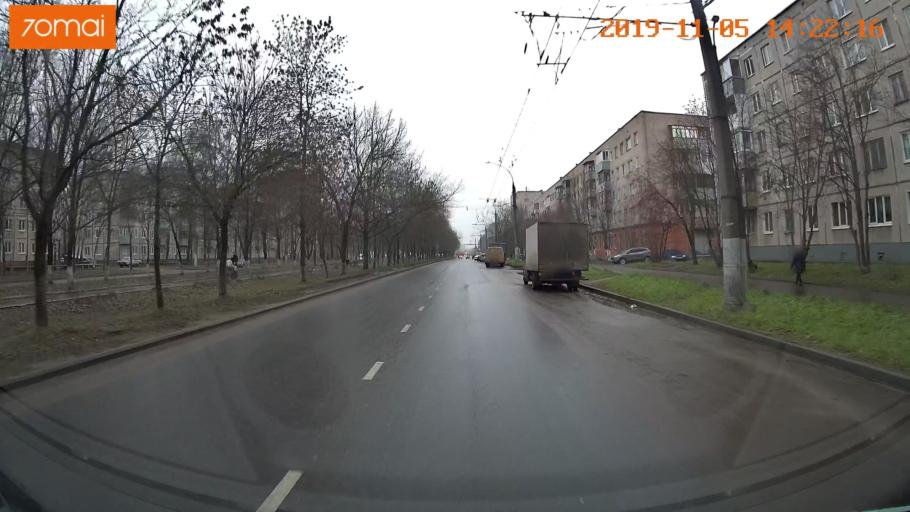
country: RU
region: Ivanovo
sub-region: Gorod Ivanovo
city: Ivanovo
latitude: 56.9624
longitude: 41.0061
